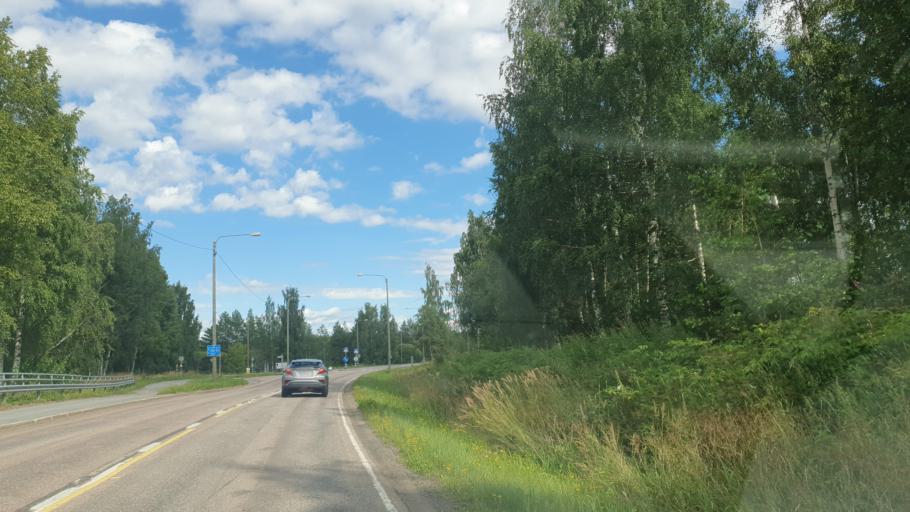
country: FI
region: Central Finland
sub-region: Jyvaeskylae
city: Saeynaetsalo
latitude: 62.1386
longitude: 25.7406
